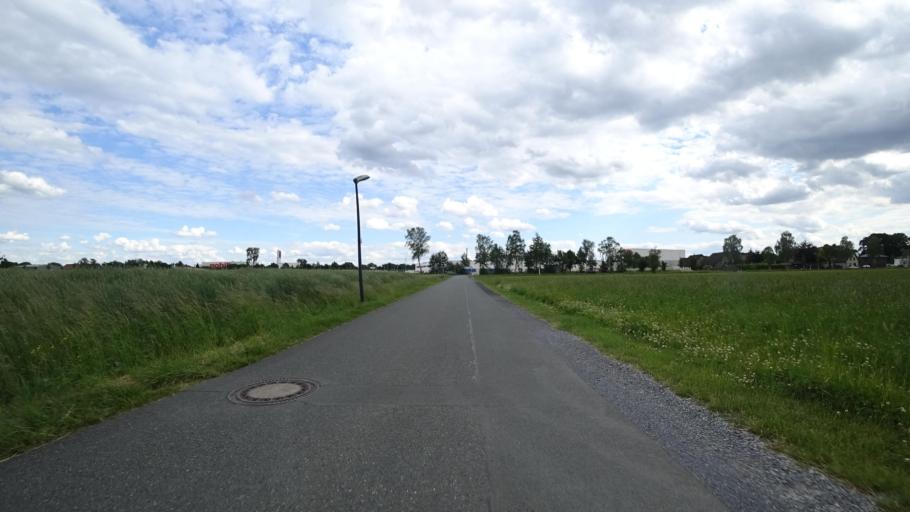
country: DE
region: North Rhine-Westphalia
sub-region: Regierungsbezirk Detmold
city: Guetersloh
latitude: 51.8931
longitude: 8.4412
